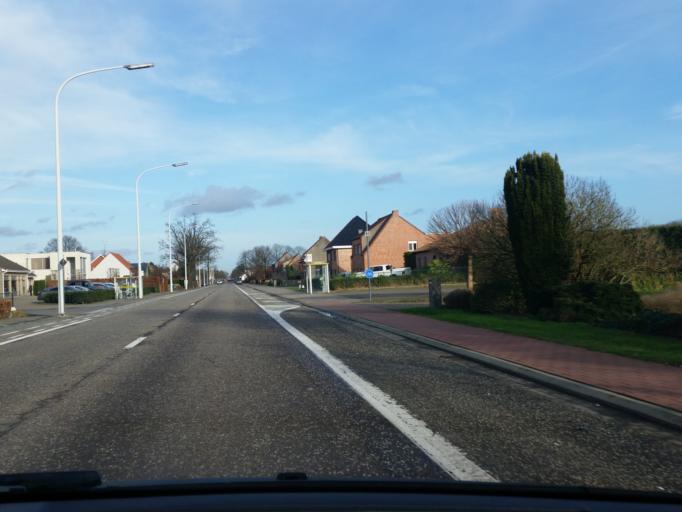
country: BE
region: Flanders
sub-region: Provincie Antwerpen
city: Wuustwezel
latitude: 51.3837
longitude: 4.5839
